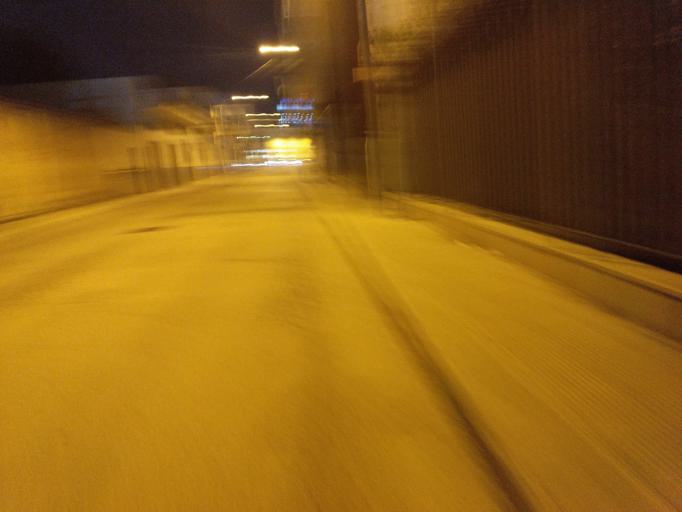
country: IT
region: Apulia
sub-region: Provincia di Bari
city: Modugno
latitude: 41.0805
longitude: 16.7847
